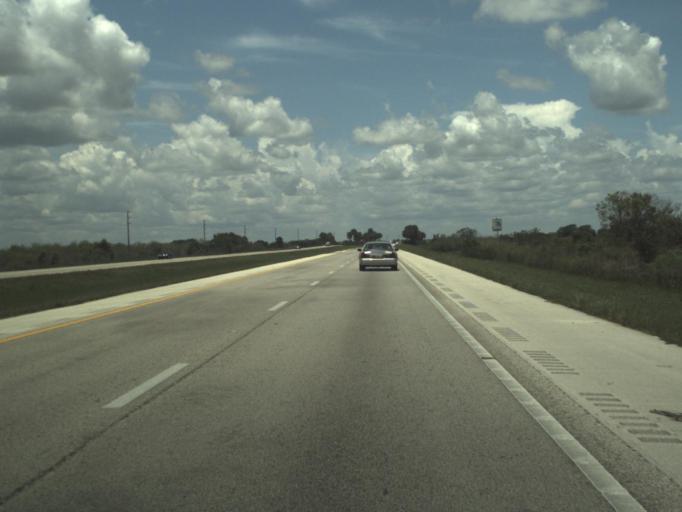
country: US
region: Florida
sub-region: Broward County
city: Weston
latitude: 26.1467
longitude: -80.6927
